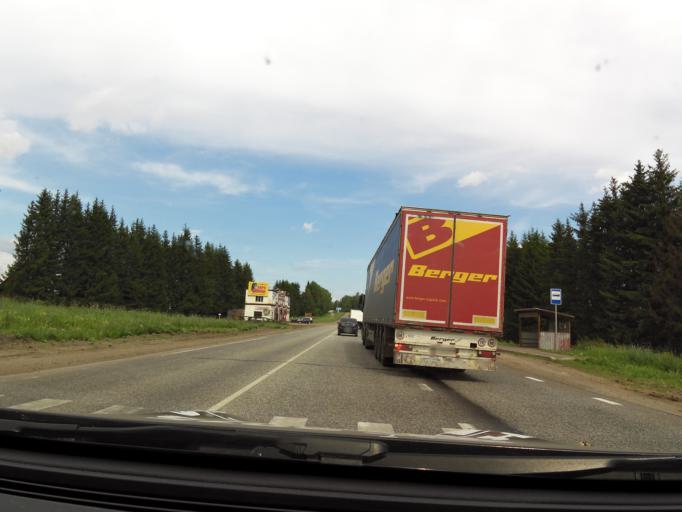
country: RU
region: Kirov
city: Stulovo
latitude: 58.7129
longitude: 50.1176
